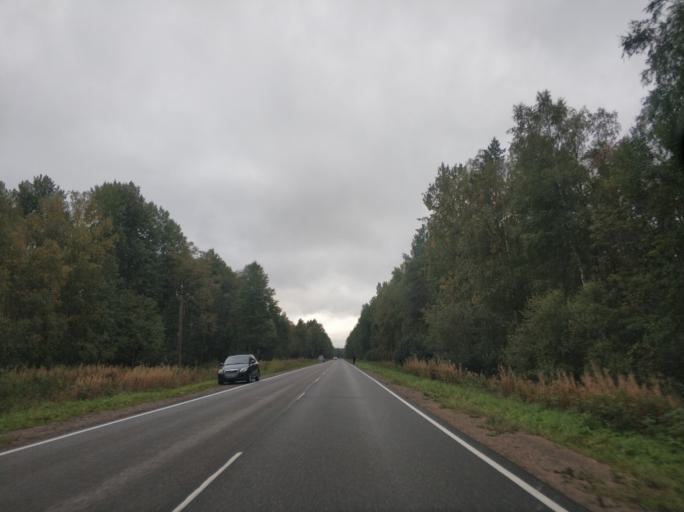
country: RU
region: Leningrad
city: Borisova Griva
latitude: 60.1250
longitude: 30.9633
